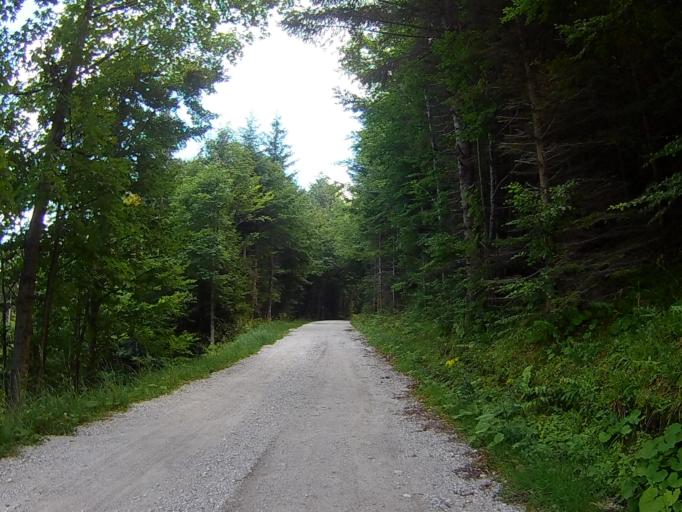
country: SI
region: Ruse
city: Ruse
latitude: 46.4995
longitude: 15.4915
